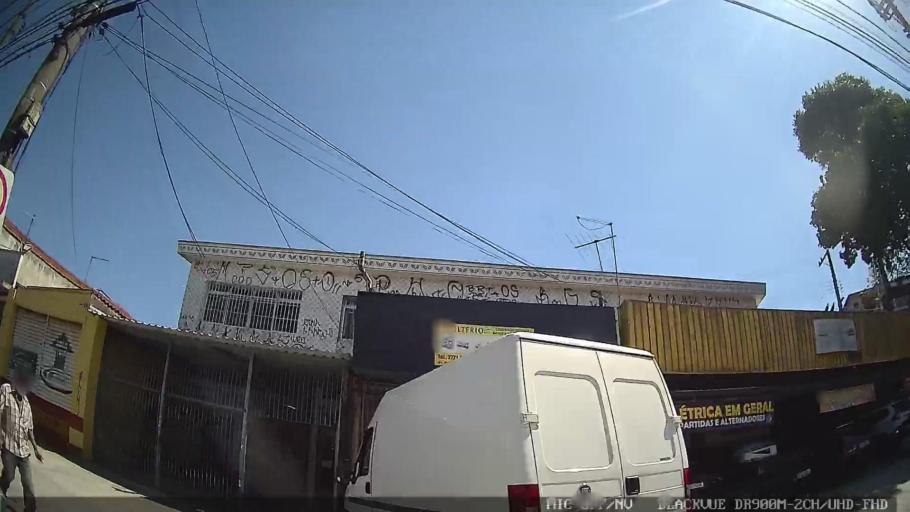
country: BR
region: Sao Paulo
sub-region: Sao Caetano Do Sul
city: Sao Caetano do Sul
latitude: -23.5836
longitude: -46.4950
